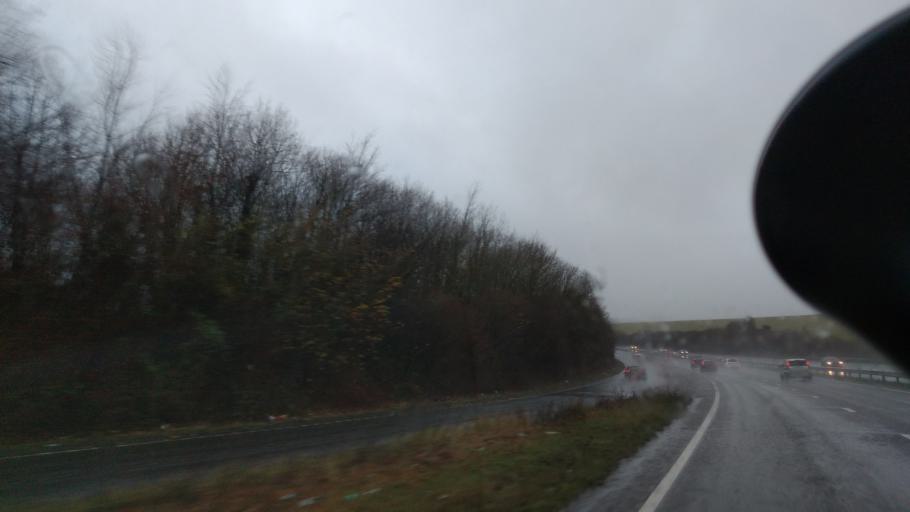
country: GB
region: England
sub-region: Brighton and Hove
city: Brighton
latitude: 50.8710
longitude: -0.1266
